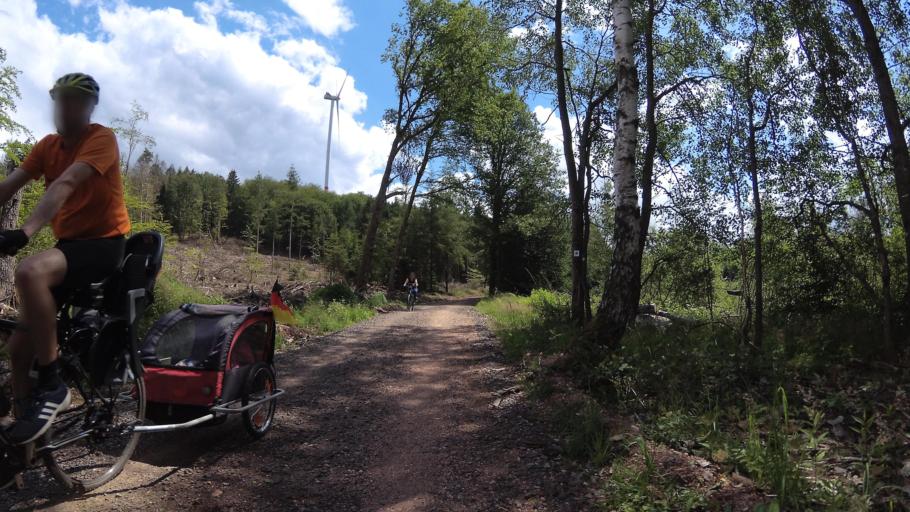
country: DE
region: Saarland
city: Oberthal
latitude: 49.5348
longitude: 7.0744
